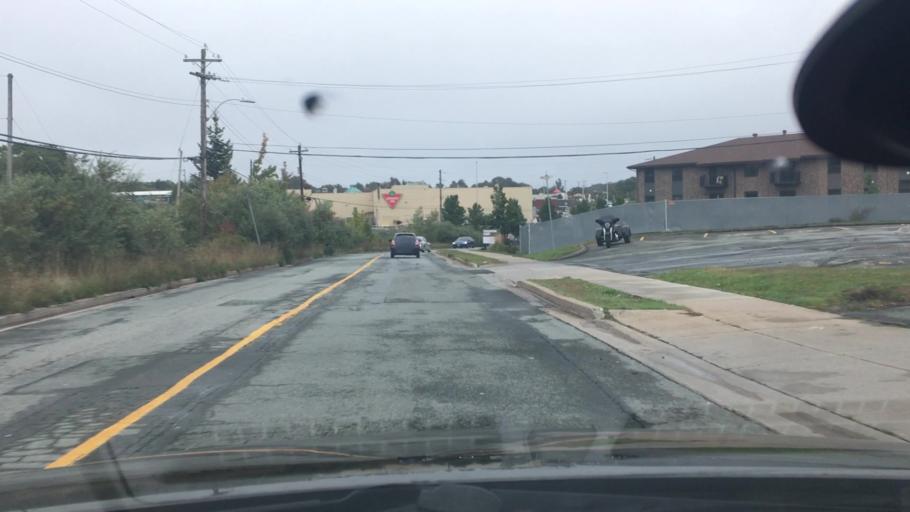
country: CA
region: Nova Scotia
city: Dartmouth
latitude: 44.7708
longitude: -63.6968
